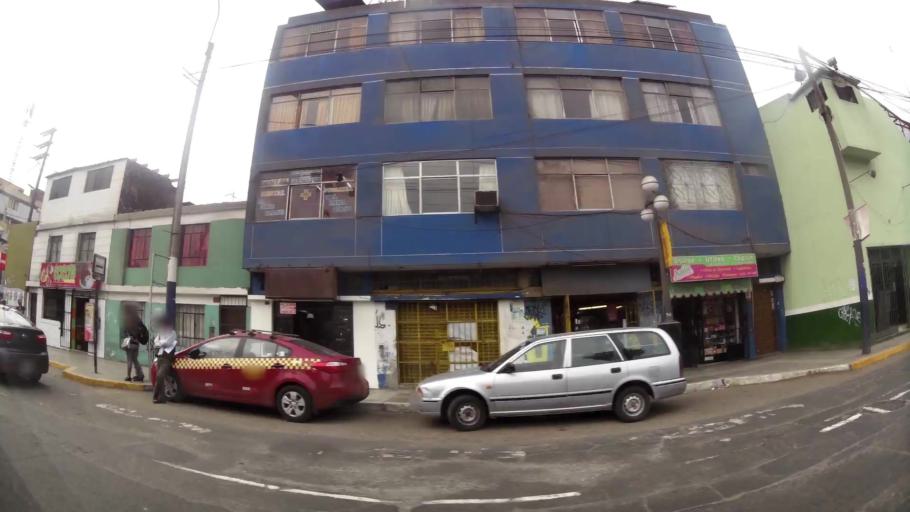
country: PE
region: Lima
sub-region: Lima
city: Surco
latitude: -12.1734
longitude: -77.0201
